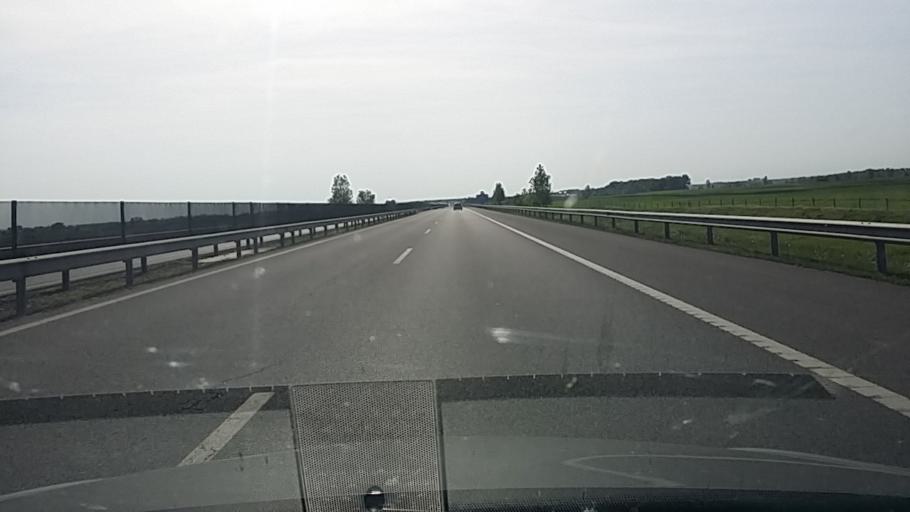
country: HU
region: Hajdu-Bihar
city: Hajdunanas
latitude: 47.8845
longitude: 21.4285
